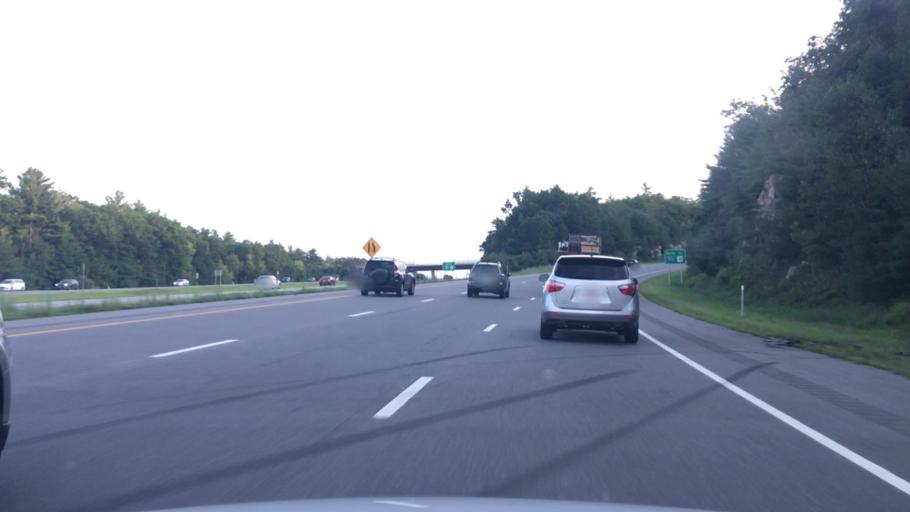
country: US
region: New Hampshire
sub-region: Merrimack County
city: Hooksett
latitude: 43.0604
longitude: -71.4718
